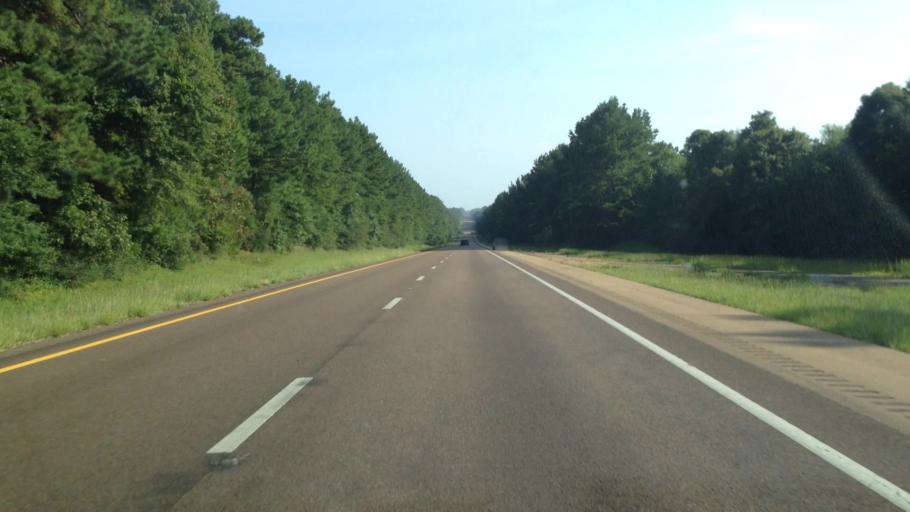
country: US
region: Mississippi
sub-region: Pike County
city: Summit
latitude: 31.3704
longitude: -90.4791
